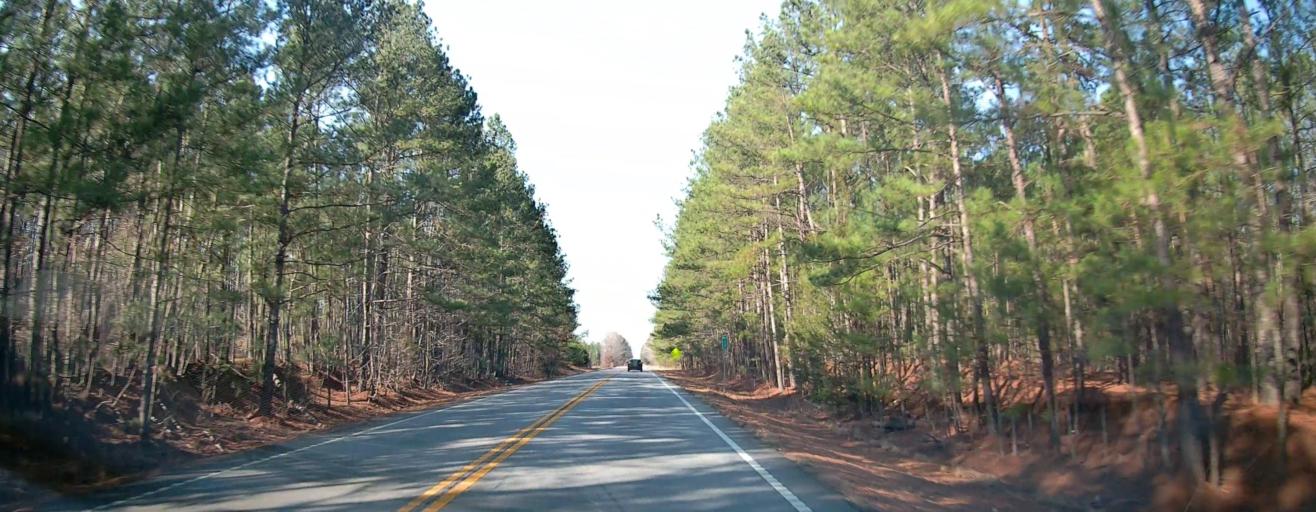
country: US
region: Georgia
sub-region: Butts County
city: Indian Springs
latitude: 33.1722
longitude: -83.8437
